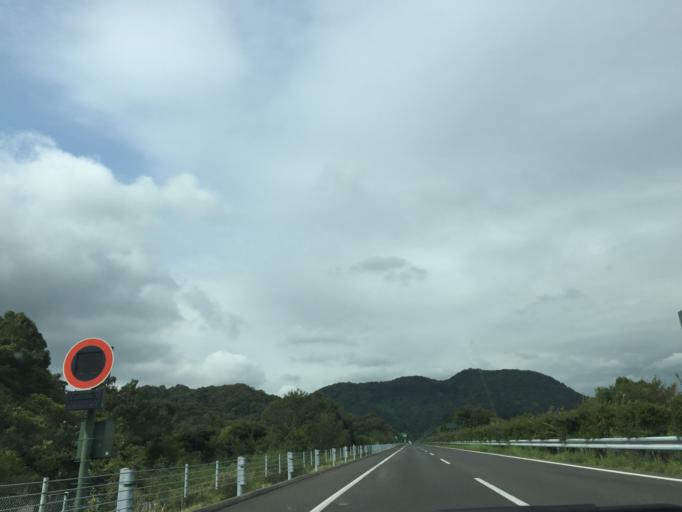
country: JP
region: Kagawa
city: Shido
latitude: 34.2762
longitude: 134.2743
